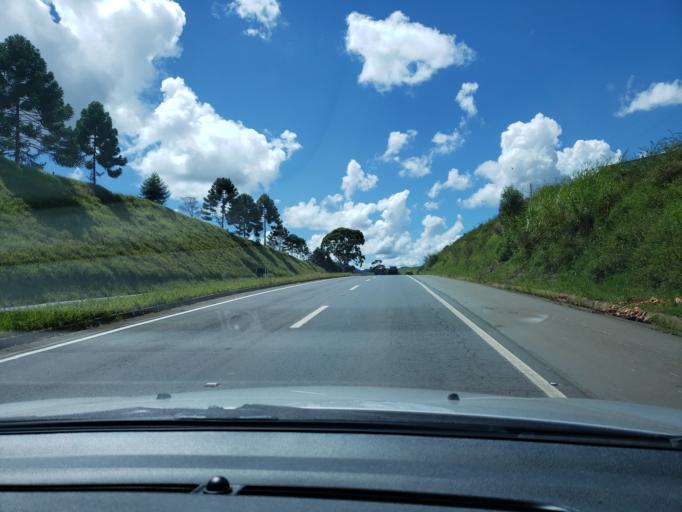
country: BR
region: Minas Gerais
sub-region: Pocos De Caldas
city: Pocos de Caldas
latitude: -21.8411
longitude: -46.6769
